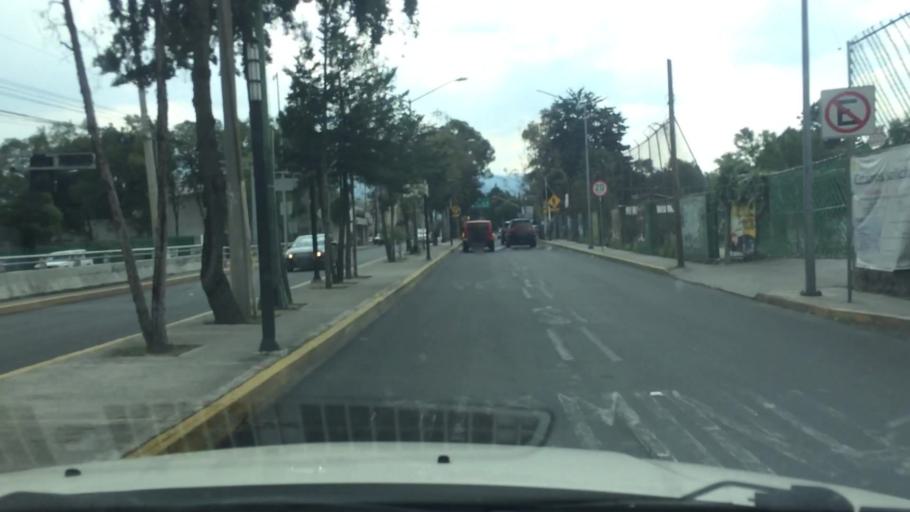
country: MX
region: Mexico City
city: Magdalena Contreras
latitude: 19.3445
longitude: -99.2403
